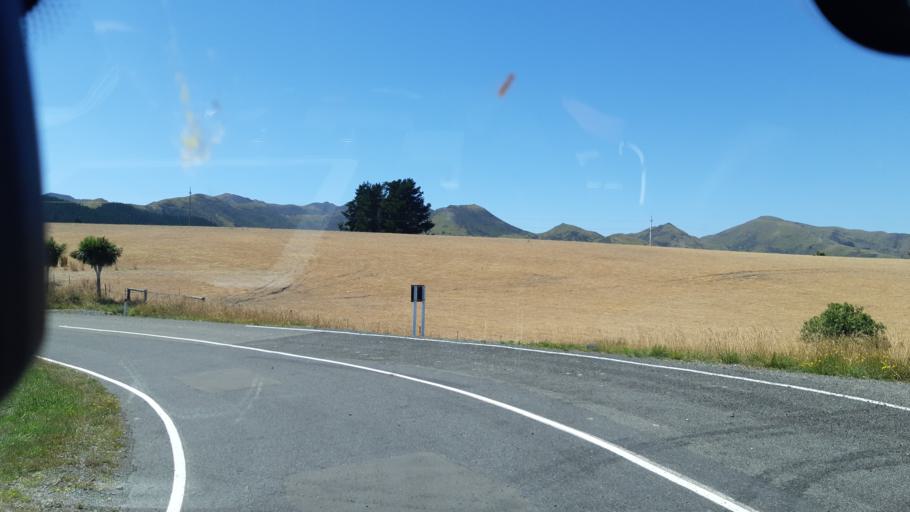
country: NZ
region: Canterbury
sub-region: Kaikoura District
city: Kaikoura
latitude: -42.6641
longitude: 173.3150
